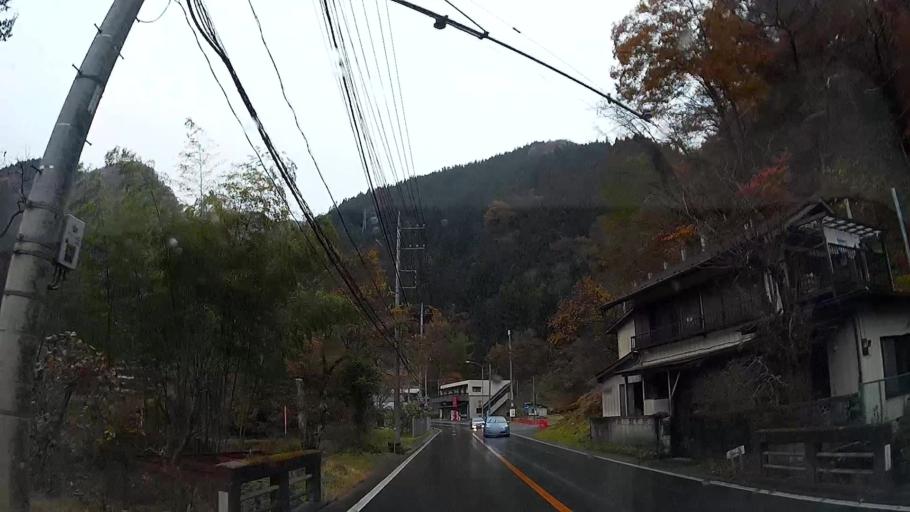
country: JP
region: Saitama
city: Chichibu
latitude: 35.9511
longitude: 138.9391
